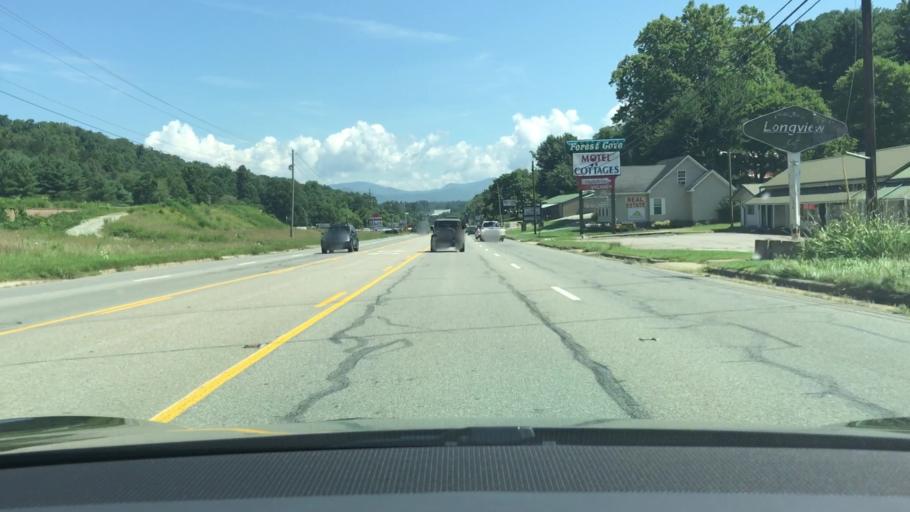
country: US
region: North Carolina
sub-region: Macon County
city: Franklin
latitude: 35.1439
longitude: -83.3963
